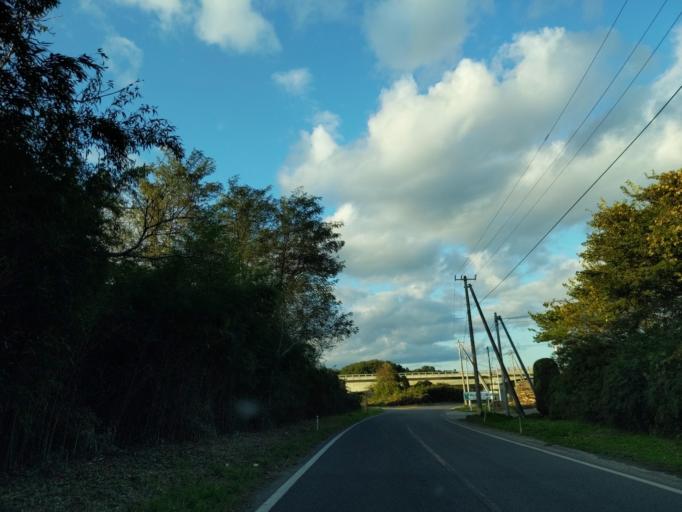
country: JP
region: Fukushima
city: Koriyama
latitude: 37.4412
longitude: 140.4237
